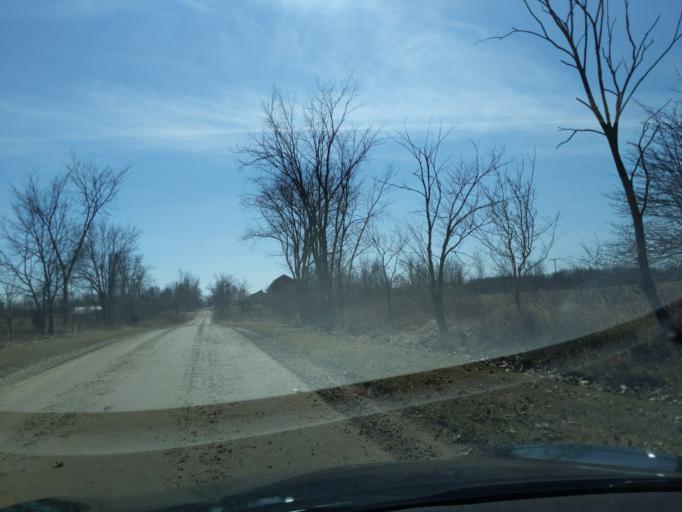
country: US
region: Michigan
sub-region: Ionia County
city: Lake Odessa
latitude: 42.7234
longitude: -85.0539
